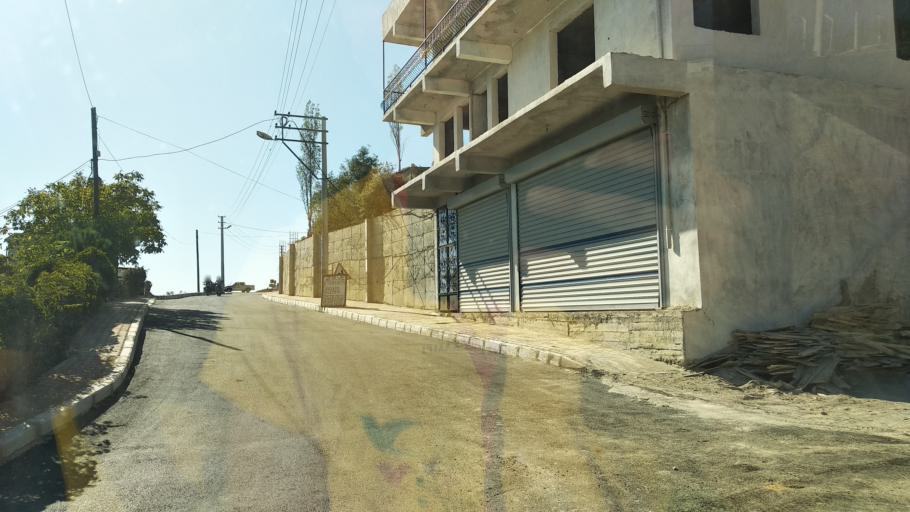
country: TR
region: Izmir
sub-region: Seferihisar
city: Seferhisar
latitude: 38.3119
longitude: 26.9563
